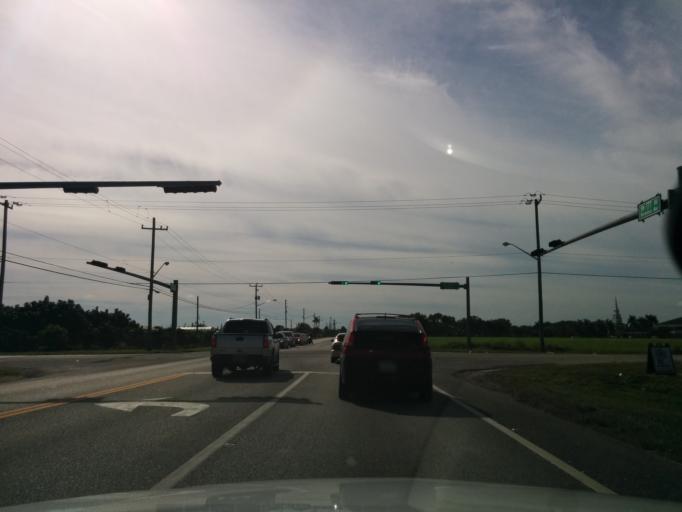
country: US
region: Florida
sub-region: Miami-Dade County
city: Homestead
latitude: 25.4995
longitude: -80.4777
